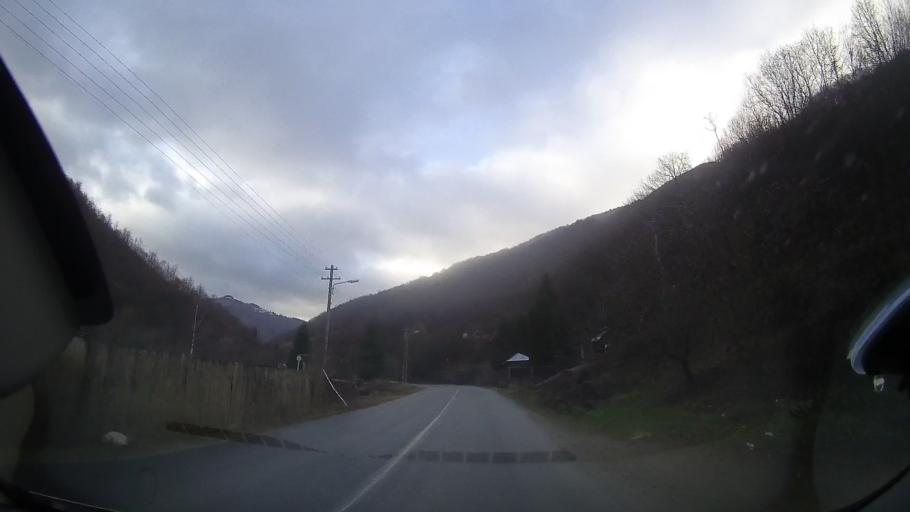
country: RO
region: Cluj
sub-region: Comuna Maguri-Racatau
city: Maguri-Racatau
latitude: 46.6806
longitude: 23.2637
